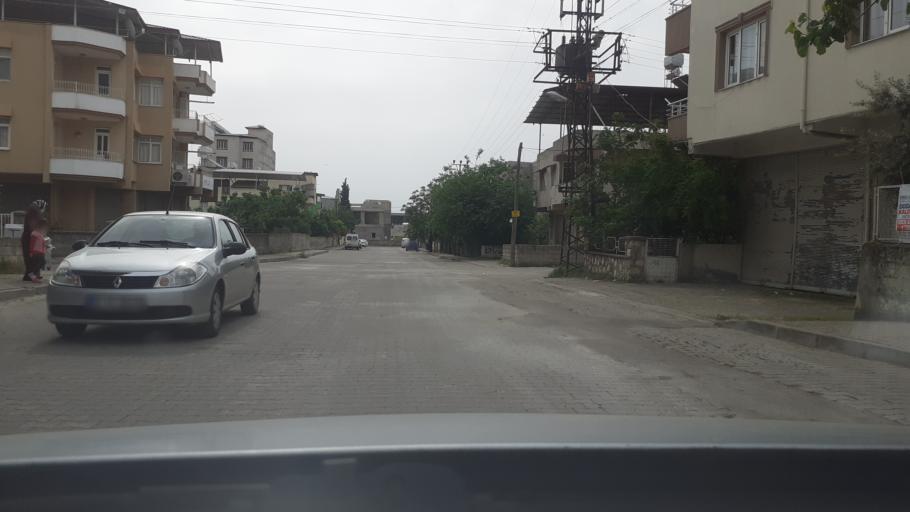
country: TR
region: Hatay
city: Kirikhan
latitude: 36.4944
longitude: 36.3655
